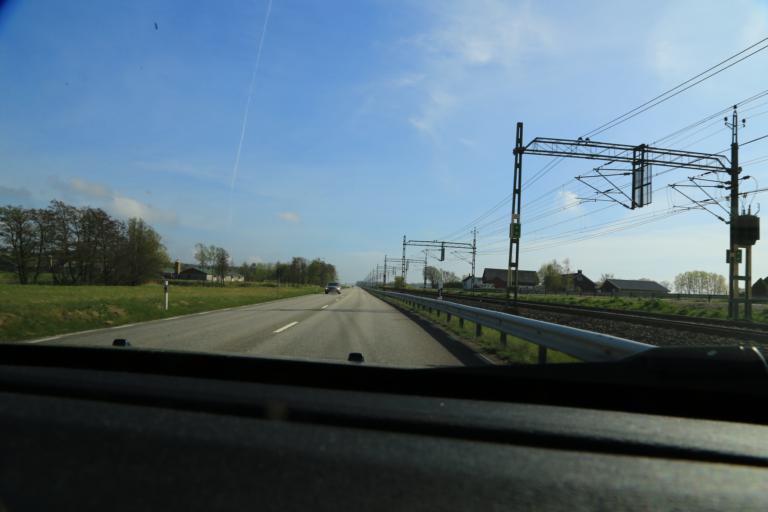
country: SE
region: Halland
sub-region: Varbergs Kommun
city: Varberg
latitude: 57.2106
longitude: 12.2217
